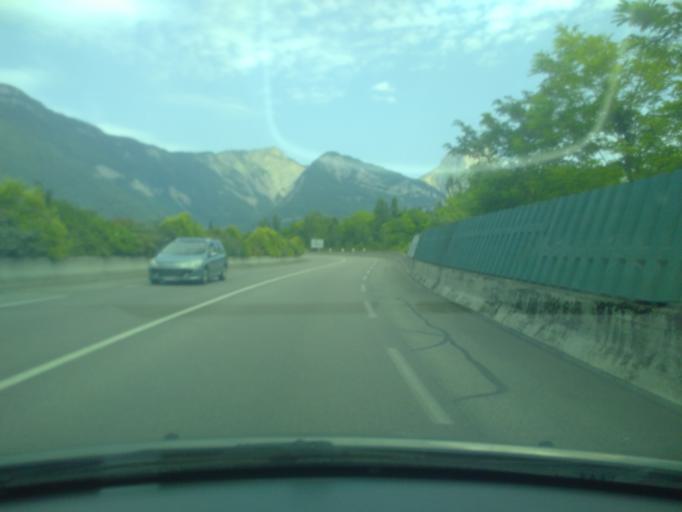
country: FR
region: Rhone-Alpes
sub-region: Departement de l'Isere
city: Saint-Nazaire-les-Eymes
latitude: 45.2478
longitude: 5.8446
